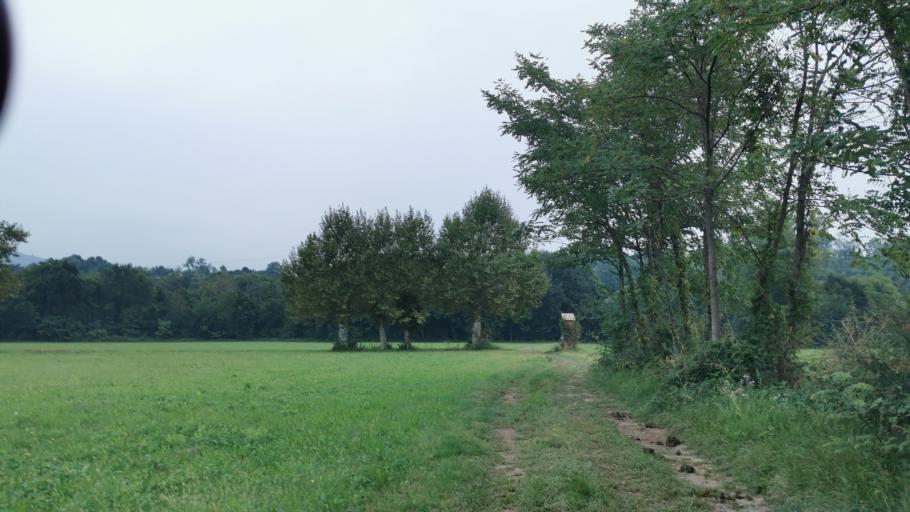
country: IT
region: Piedmont
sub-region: Provincia di Torino
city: Grosso
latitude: 45.2631
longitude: 7.5502
